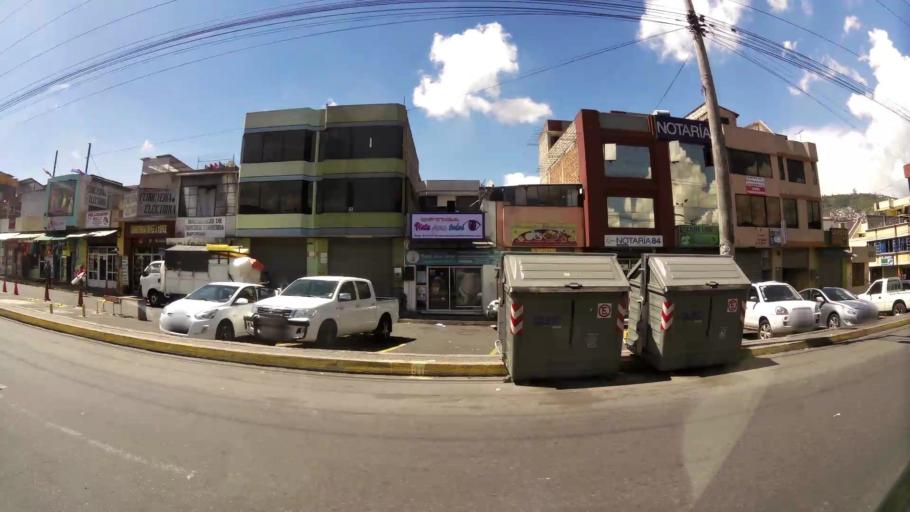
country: EC
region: Pichincha
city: Quito
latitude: -0.2683
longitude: -78.5274
